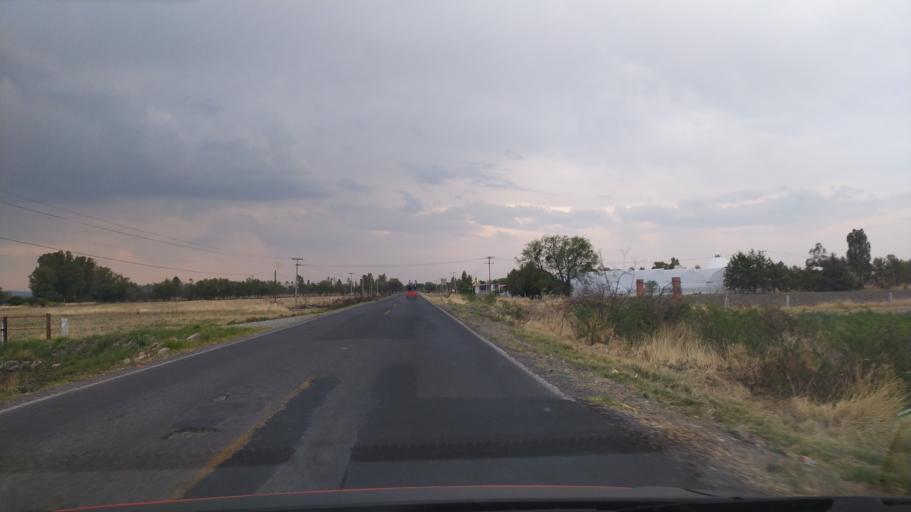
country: MX
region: Guanajuato
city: Ciudad Manuel Doblado
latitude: 20.7805
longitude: -101.9098
